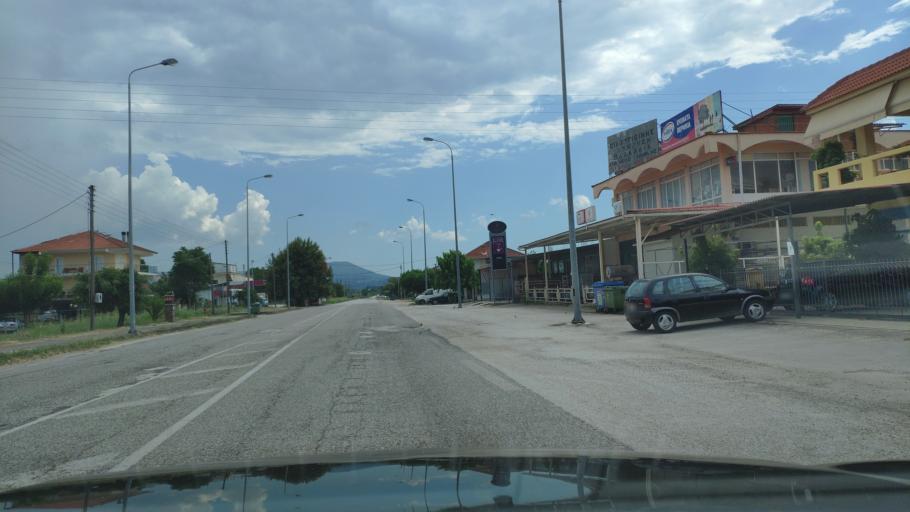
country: GR
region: West Greece
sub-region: Nomos Aitolias kai Akarnanias
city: Krikellos
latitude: 38.9471
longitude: 21.1763
